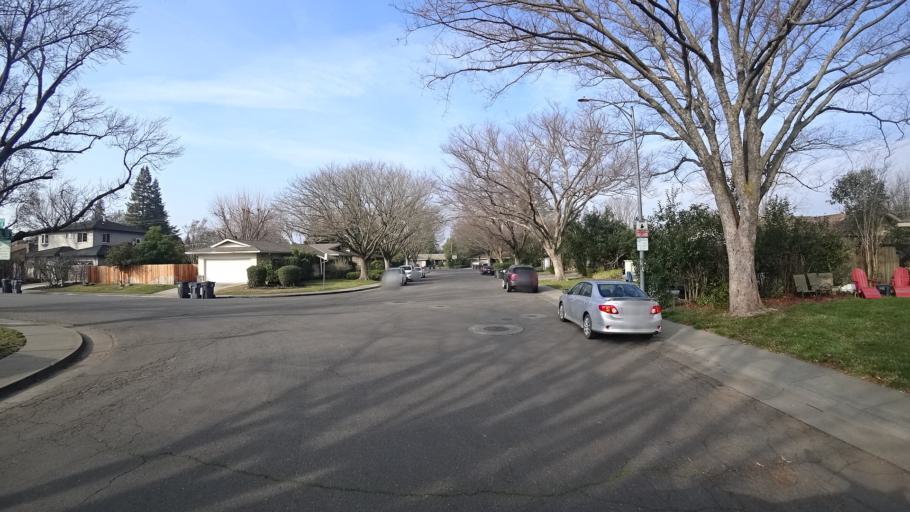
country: US
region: California
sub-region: Yolo County
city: Davis
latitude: 38.5534
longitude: -121.7658
